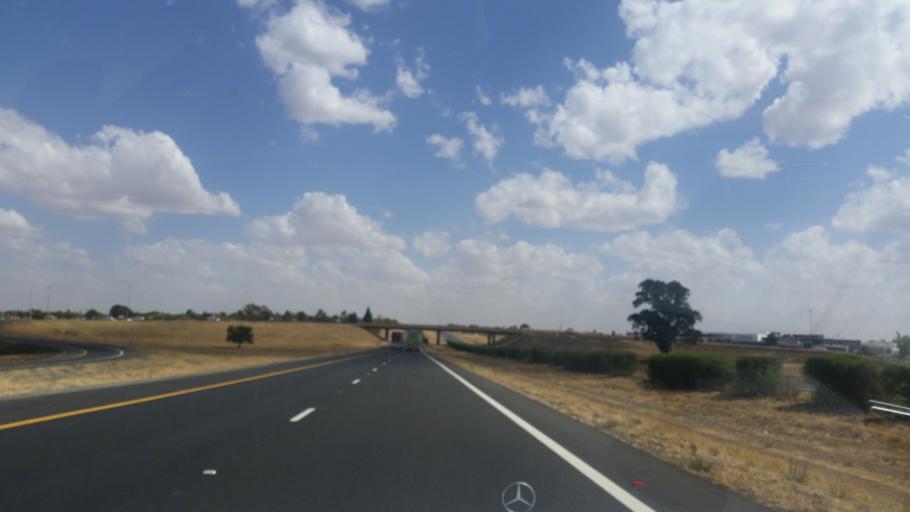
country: ZA
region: Orange Free State
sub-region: Mangaung Metropolitan Municipality
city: Bloemfontein
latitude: -29.0880
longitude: 26.1729
